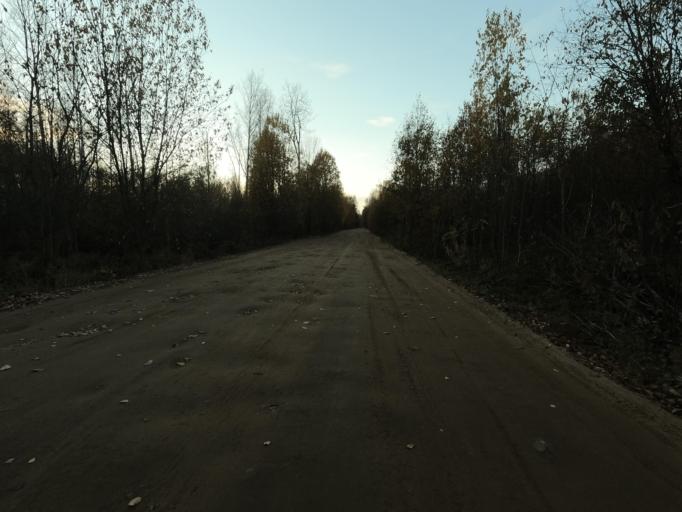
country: RU
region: Leningrad
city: Mga
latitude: 59.7565
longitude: 31.2751
